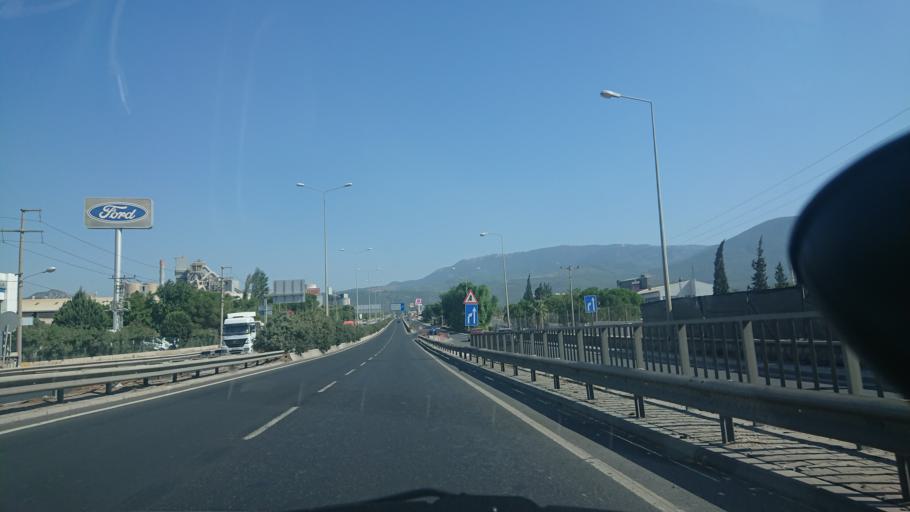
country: TR
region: Izmir
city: Bornova
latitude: 38.4565
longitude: 27.2544
